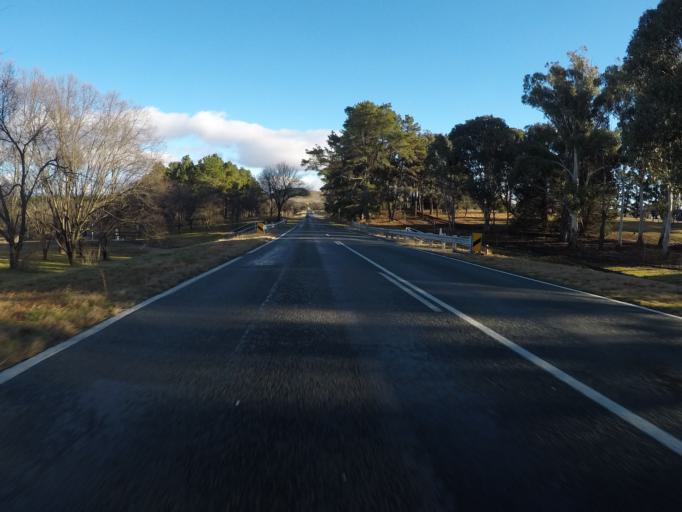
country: AU
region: Australian Capital Territory
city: Acton
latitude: -35.3085
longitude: 149.0767
